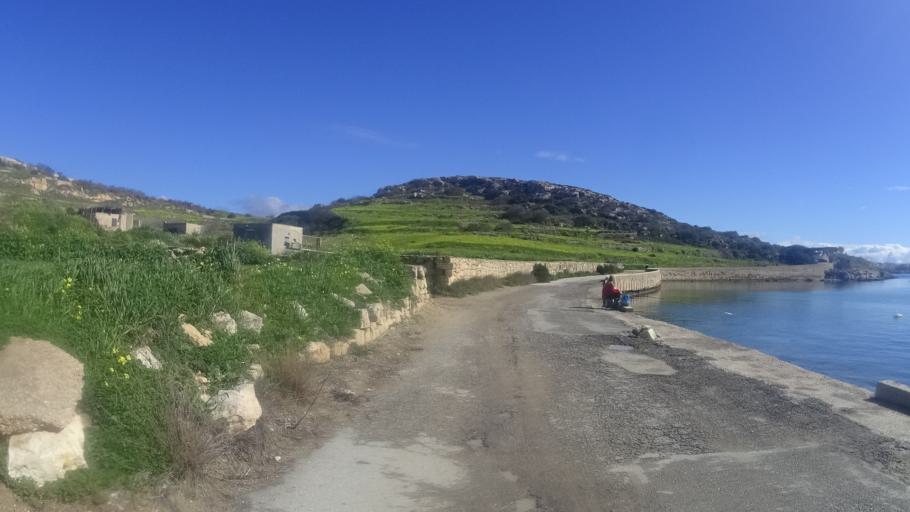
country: MT
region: Saint Paul's Bay
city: San Pawl il-Bahar
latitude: 35.9594
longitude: 14.3905
